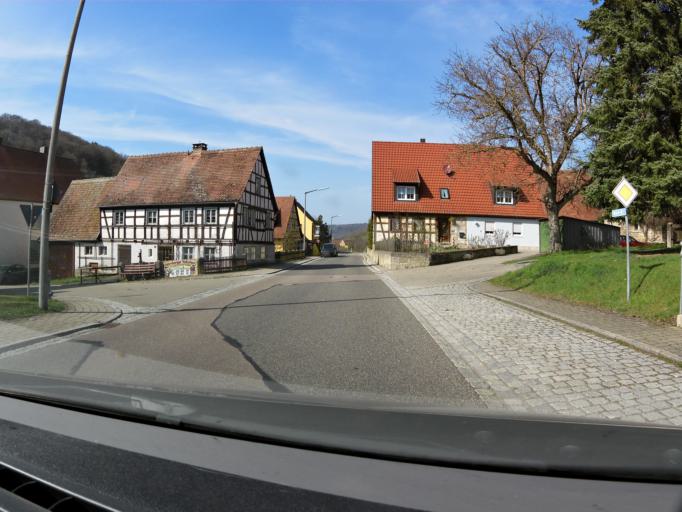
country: DE
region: Bavaria
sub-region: Regierungsbezirk Mittelfranken
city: Adelshofen
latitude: 49.4163
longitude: 10.1516
